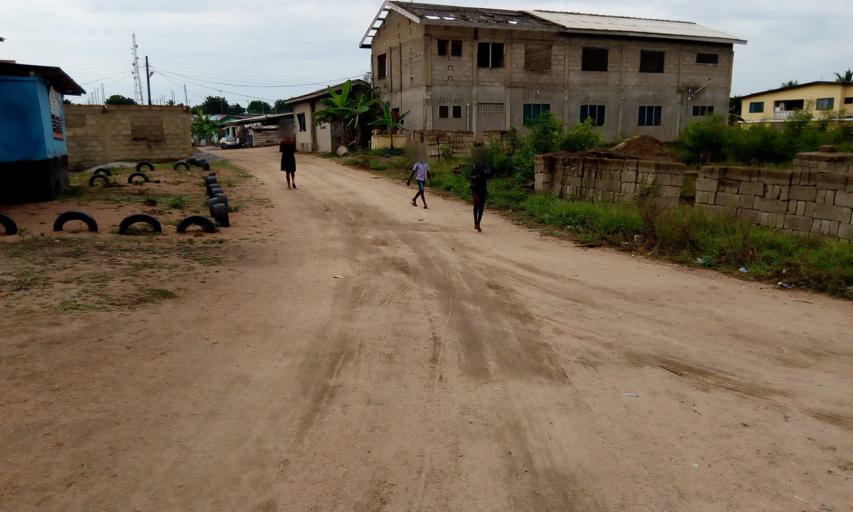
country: GH
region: Central
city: Winneba
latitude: 5.3575
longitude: -0.6206
